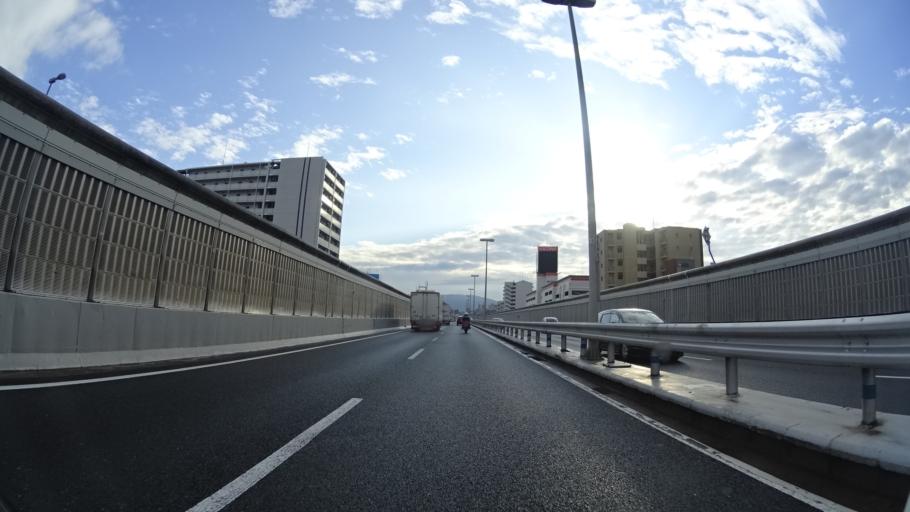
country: JP
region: Osaka
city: Moriguchi
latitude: 34.6784
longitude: 135.5643
